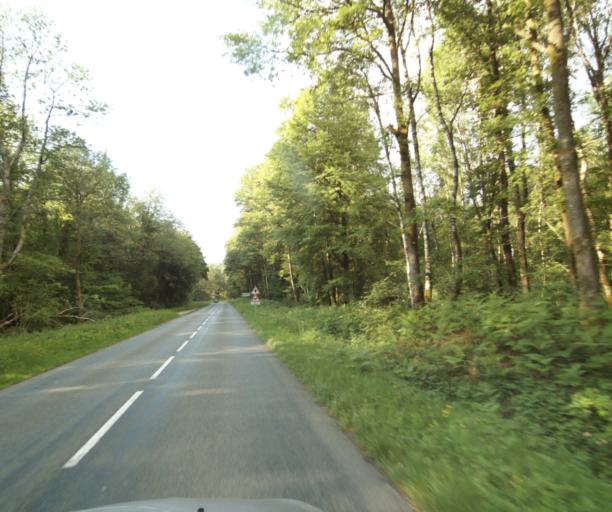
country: FR
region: Champagne-Ardenne
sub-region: Departement des Ardennes
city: Nouzonville
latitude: 49.8253
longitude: 4.6978
